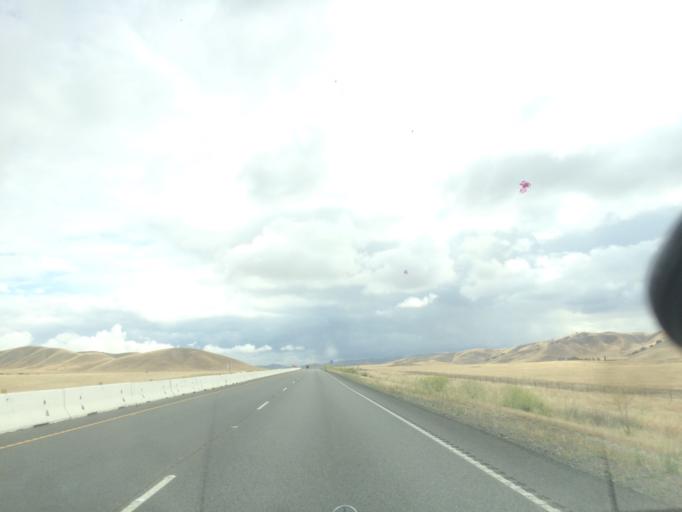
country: US
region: California
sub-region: San Luis Obispo County
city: Shandon
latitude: 35.7070
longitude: -120.3163
